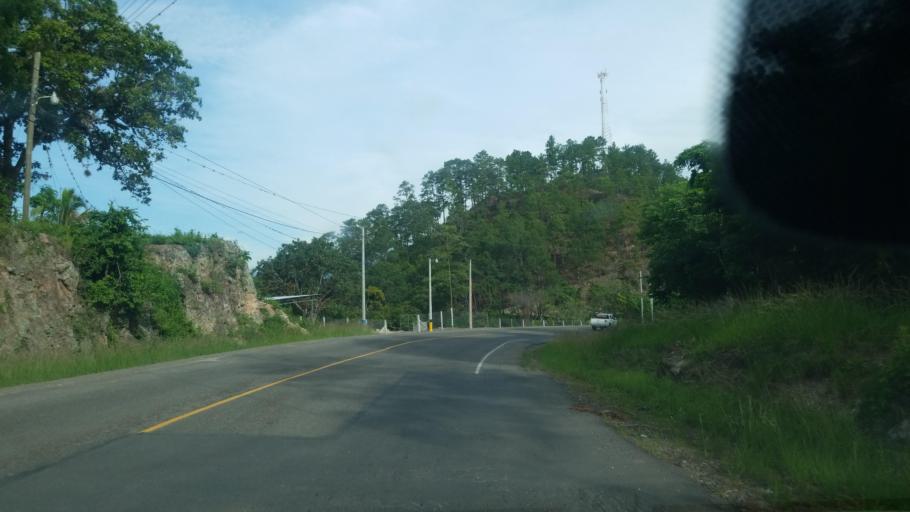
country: HN
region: Santa Barbara
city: Trinidad
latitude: 15.1632
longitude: -88.2602
